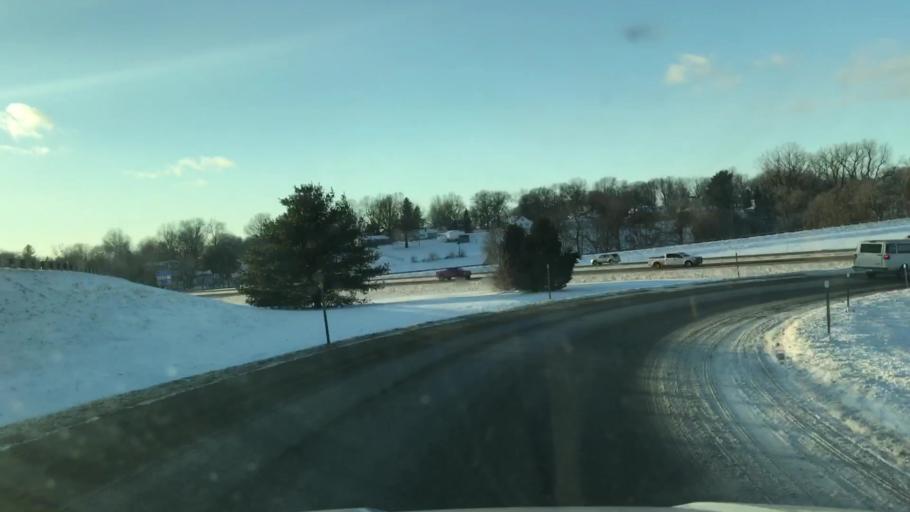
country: US
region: Missouri
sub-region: Buchanan County
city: Saint Joseph
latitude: 39.7479
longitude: -94.7906
